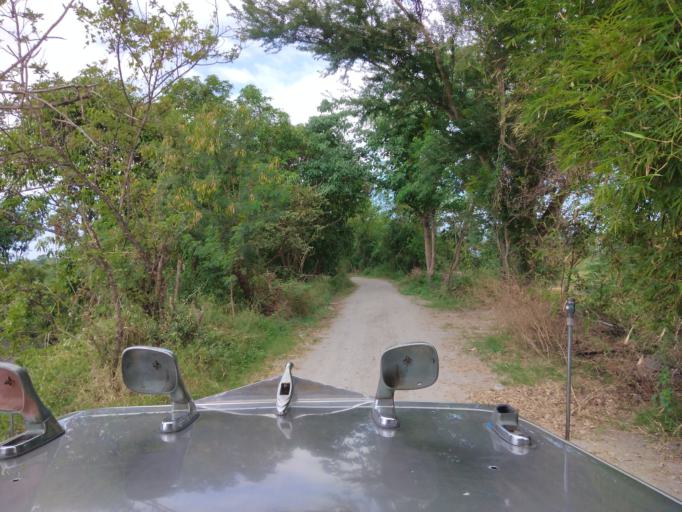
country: PH
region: Central Luzon
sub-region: Province of Pampanga
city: San Patricio
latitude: 15.1130
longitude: 120.7182
